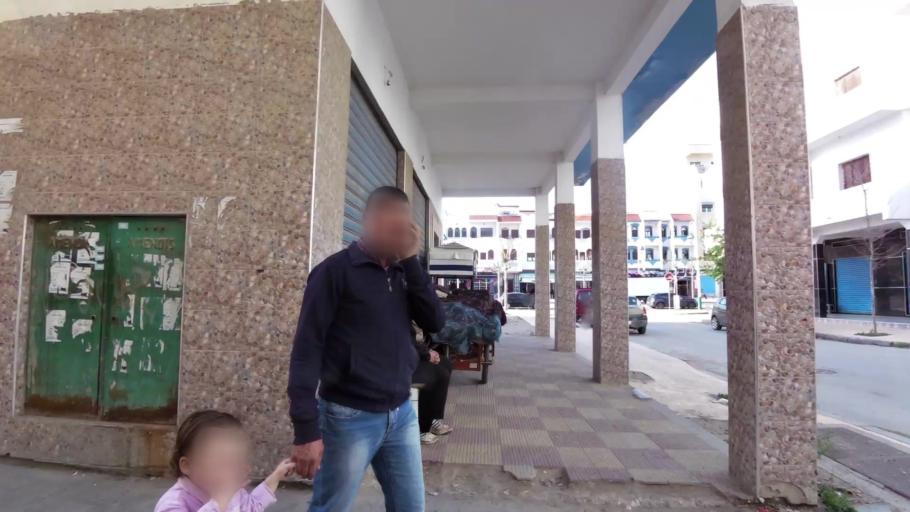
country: MA
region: Tanger-Tetouan
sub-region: Tetouan
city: Martil
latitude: 35.6139
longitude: -5.2818
